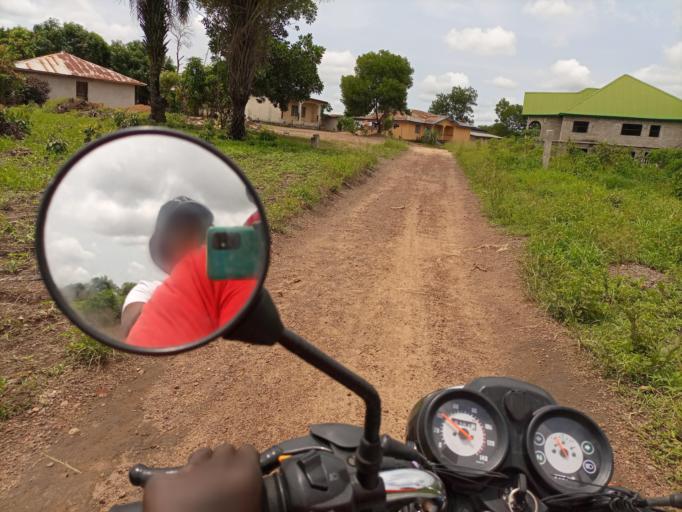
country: SL
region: Southern Province
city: Baoma
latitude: 7.9771
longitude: -11.7178
